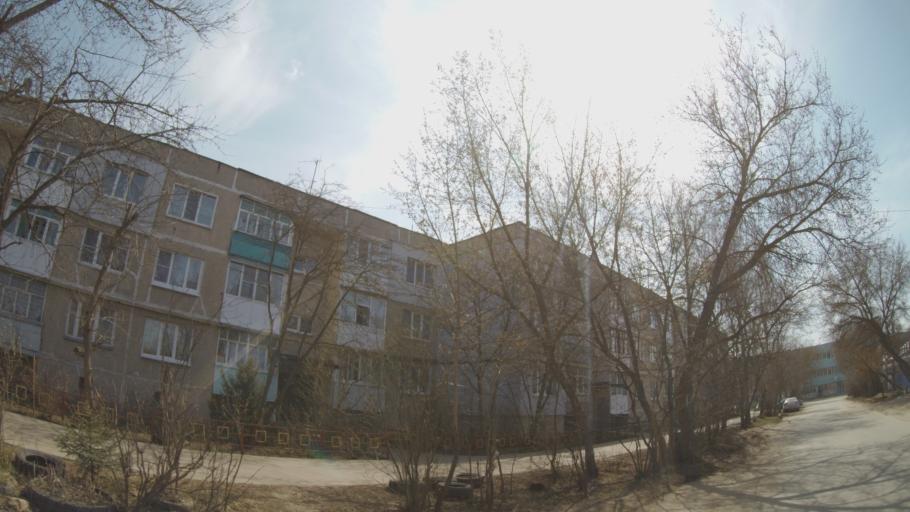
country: RU
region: Nizjnij Novgorod
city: Vyyezdnoye
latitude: 55.3850
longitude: 43.8114
